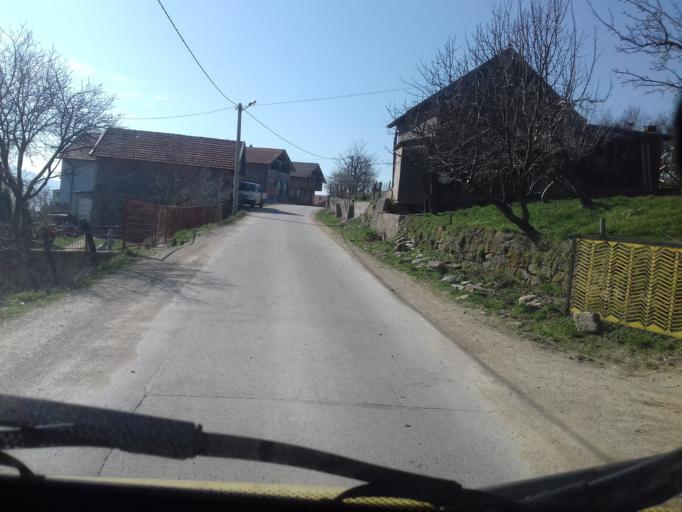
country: BA
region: Federation of Bosnia and Herzegovina
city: Travnik
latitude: 44.2518
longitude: 17.7352
